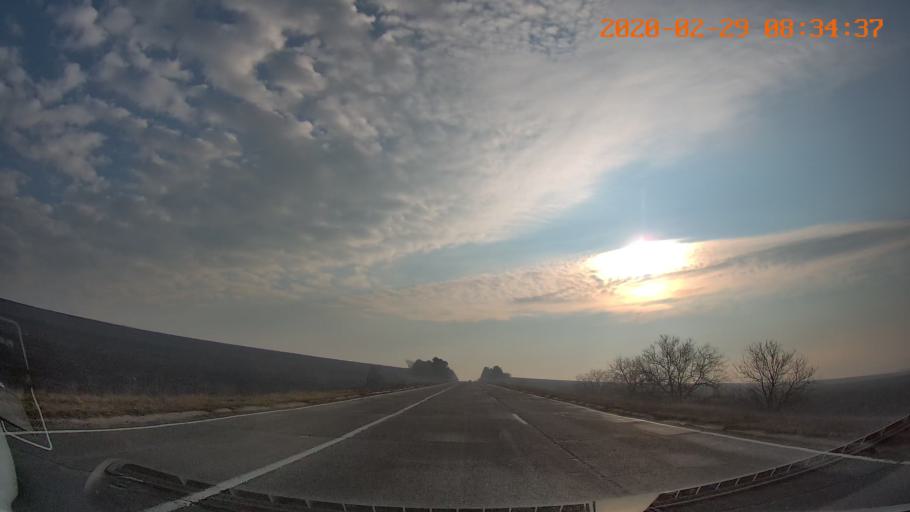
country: MD
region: Anenii Noi
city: Anenii Noi
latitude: 46.9244
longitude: 29.3124
